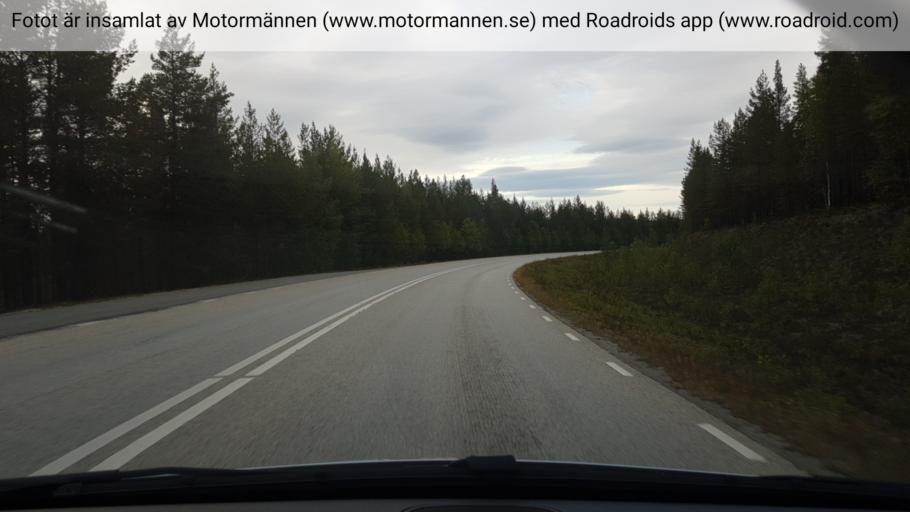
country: SE
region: Jaemtland
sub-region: Harjedalens Kommun
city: Sveg
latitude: 62.4141
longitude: 13.7680
